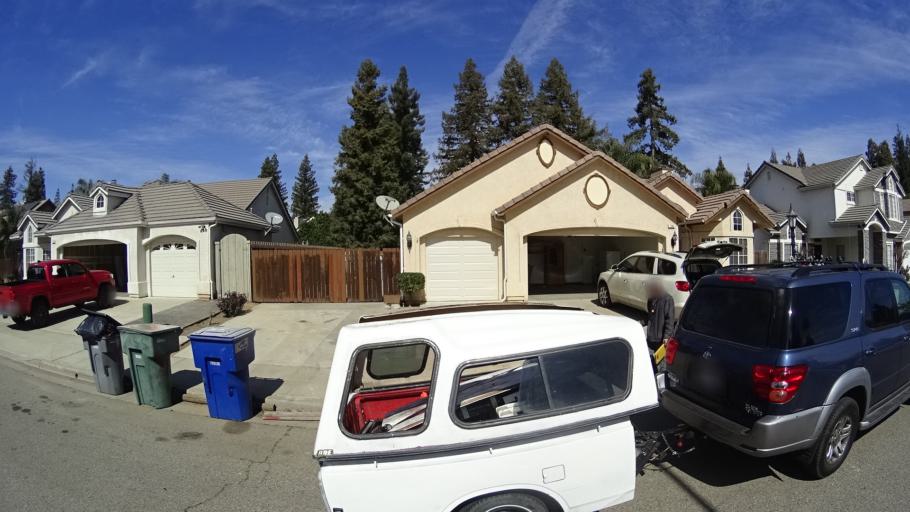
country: US
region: California
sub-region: Fresno County
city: Clovis
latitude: 36.8552
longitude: -119.7691
